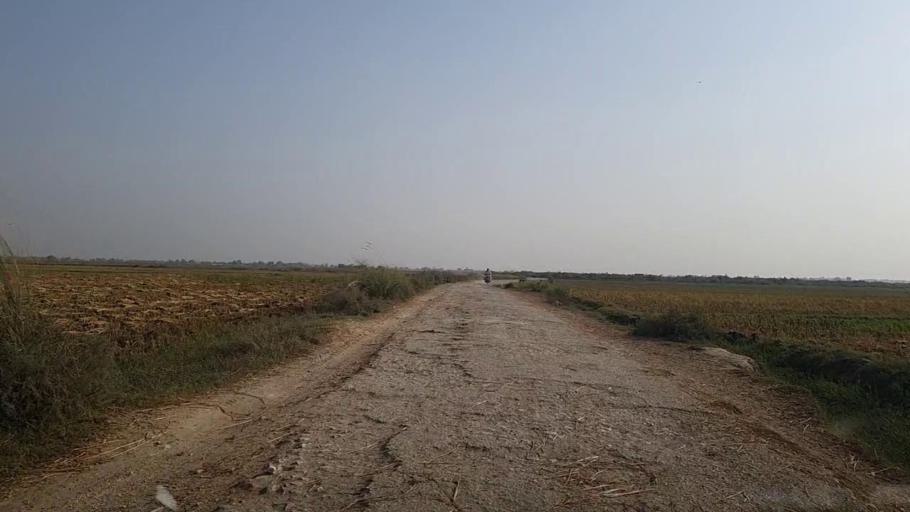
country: PK
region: Sindh
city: Kandhkot
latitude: 28.2979
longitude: 69.2522
